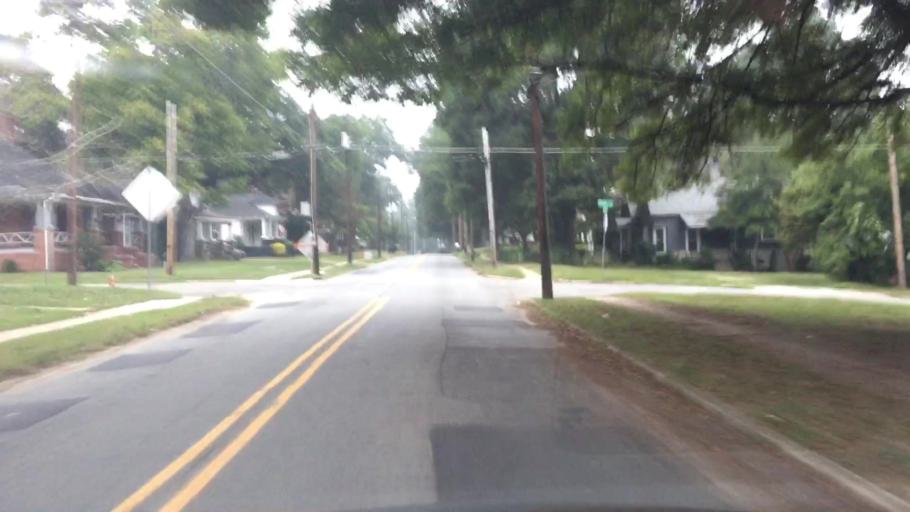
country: US
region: North Carolina
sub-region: Iredell County
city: Mooresville
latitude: 35.5897
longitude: -80.8047
